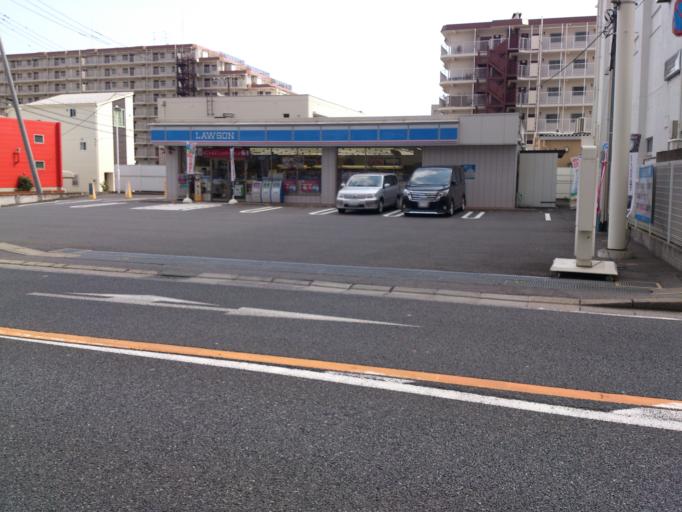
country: JP
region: Chiba
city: Funabashi
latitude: 35.6865
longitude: 140.0052
